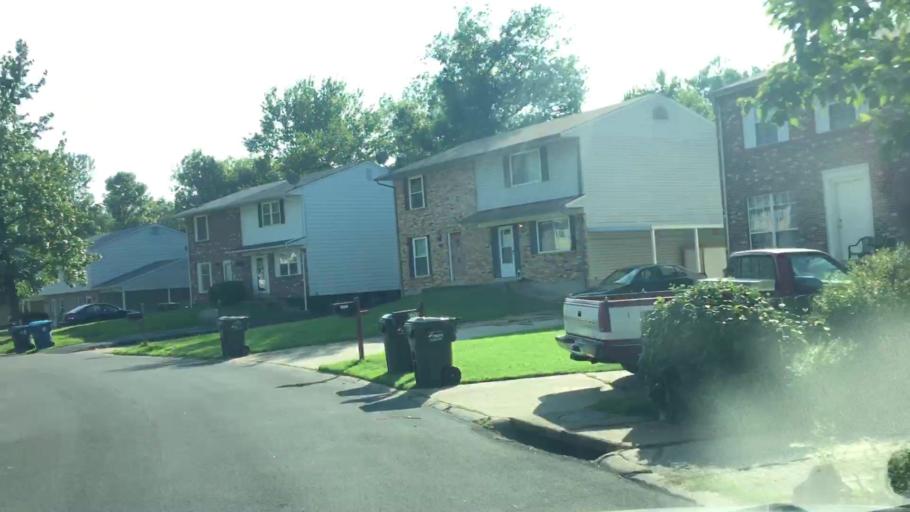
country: US
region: Missouri
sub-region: Jefferson County
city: Arnold
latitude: 38.4486
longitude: -90.3605
